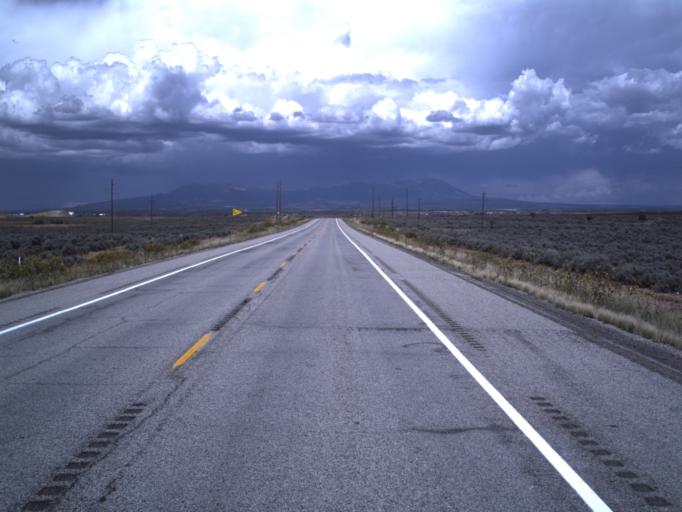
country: US
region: Utah
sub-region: San Juan County
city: Blanding
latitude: 37.5174
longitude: -109.4941
